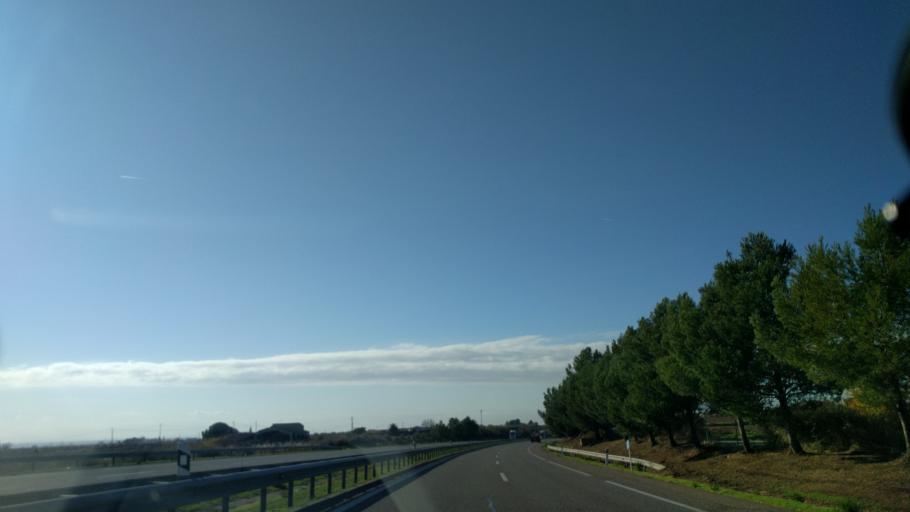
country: ES
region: Catalonia
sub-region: Provincia de Lleida
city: Alpicat
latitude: 41.6190
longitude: 0.5497
